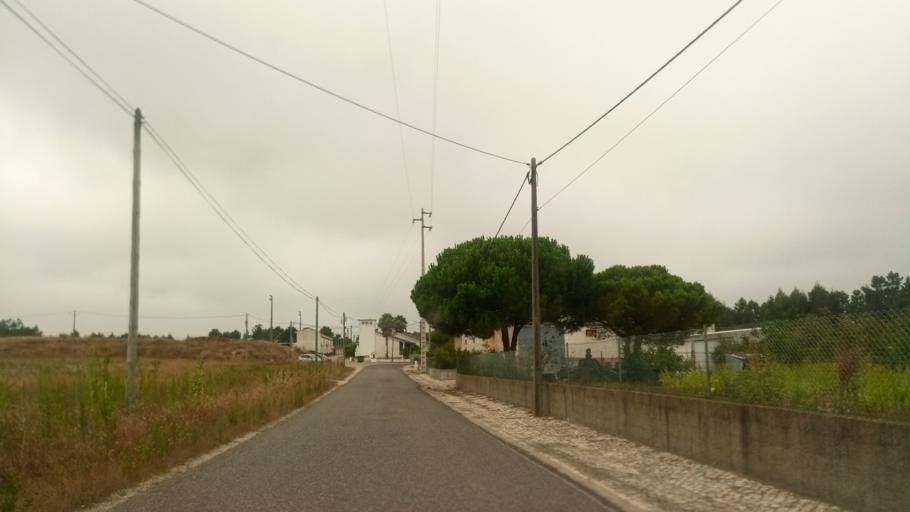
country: PT
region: Leiria
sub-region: Caldas da Rainha
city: Caldas da Rainha
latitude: 39.4272
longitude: -9.1535
